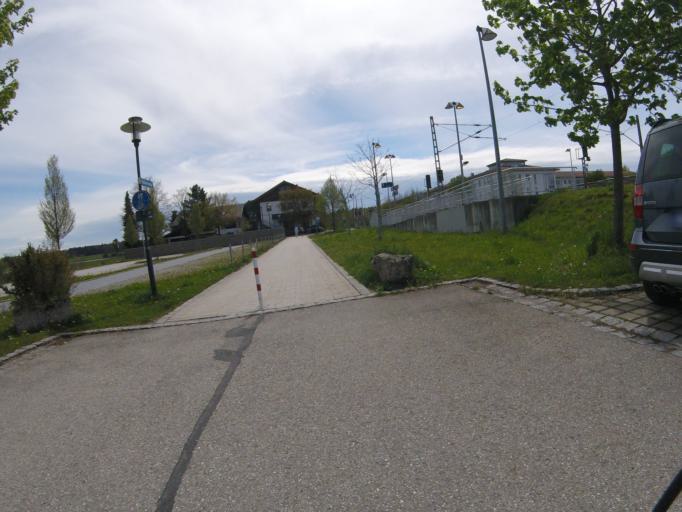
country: DE
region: Bavaria
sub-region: Upper Bavaria
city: Hohenkirchen-Siegertsbrunn
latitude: 48.0177
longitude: 11.7199
